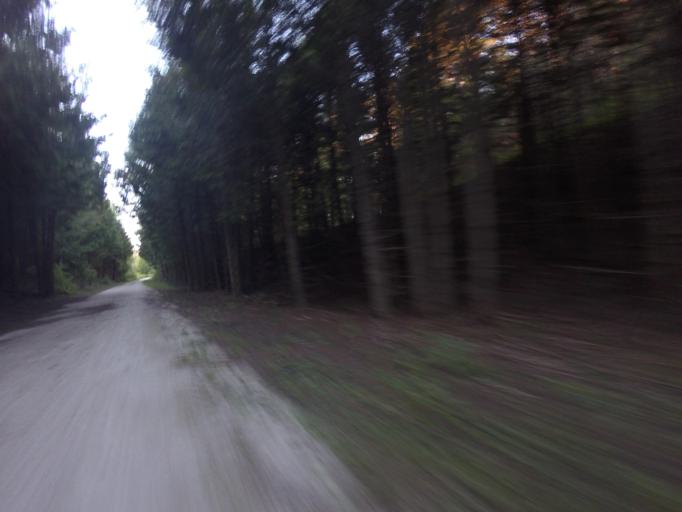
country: CA
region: Ontario
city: Orangeville
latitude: 43.9326
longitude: -79.8440
